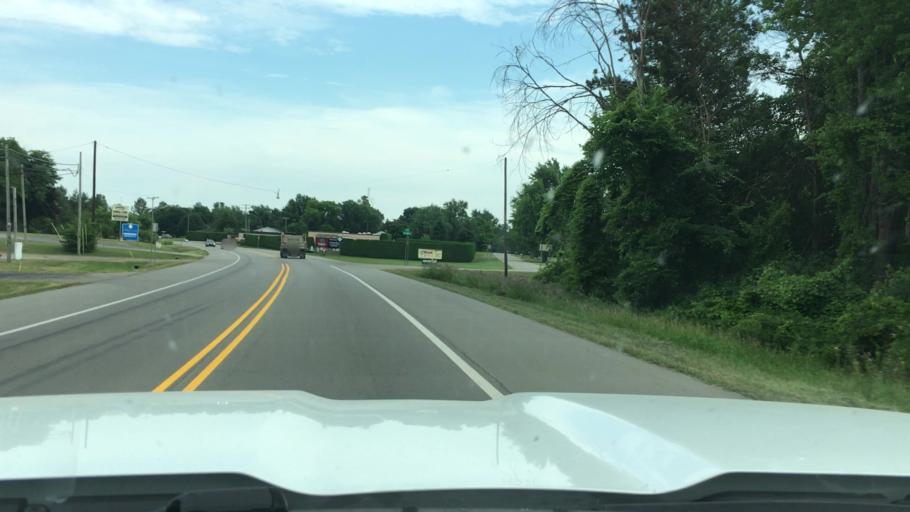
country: US
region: Michigan
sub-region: Sanilac County
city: Marlette
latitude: 43.3394
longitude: -83.0843
